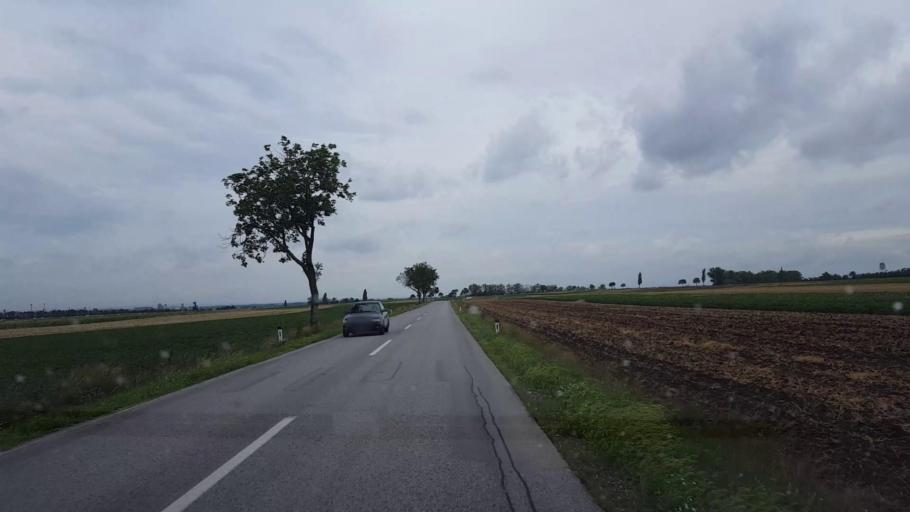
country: AT
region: Lower Austria
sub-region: Politischer Bezirk Wien-Umgebung
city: Rauchenwarth
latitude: 48.0985
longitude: 16.5266
